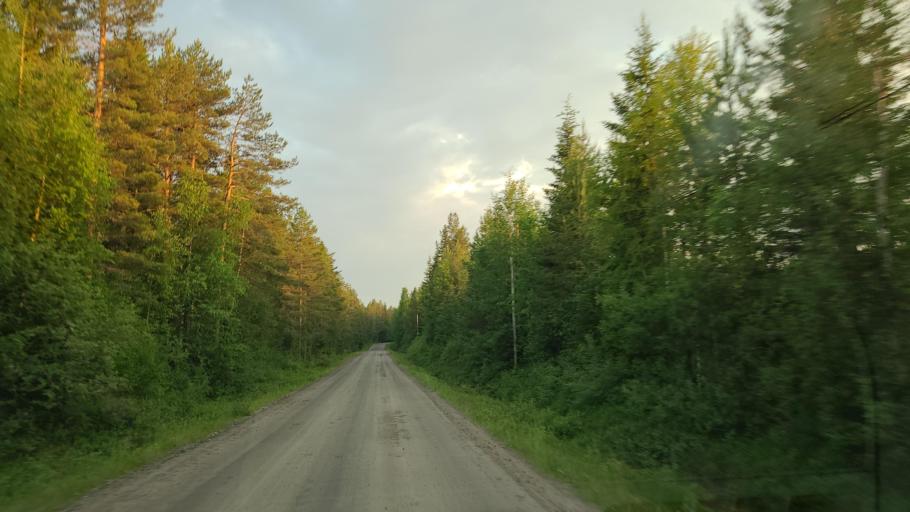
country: SE
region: Vaesterbotten
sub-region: Robertsfors Kommun
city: Robertsfors
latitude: 64.0734
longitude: 20.8828
